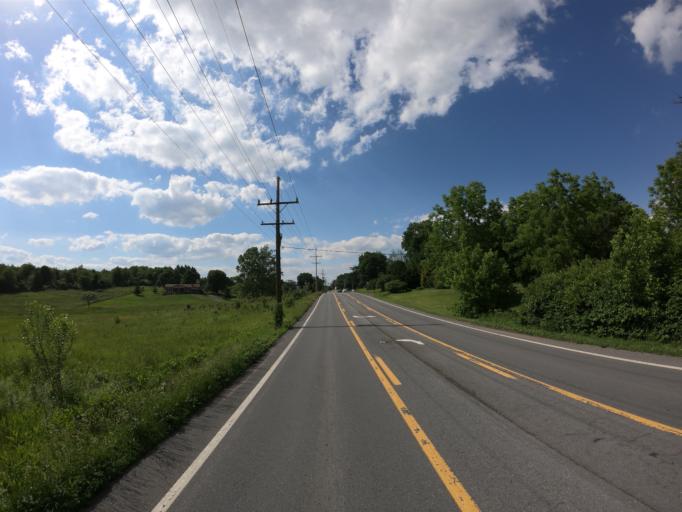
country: US
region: West Virginia
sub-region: Berkeley County
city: Martinsburg
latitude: 39.4155
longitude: -77.9181
